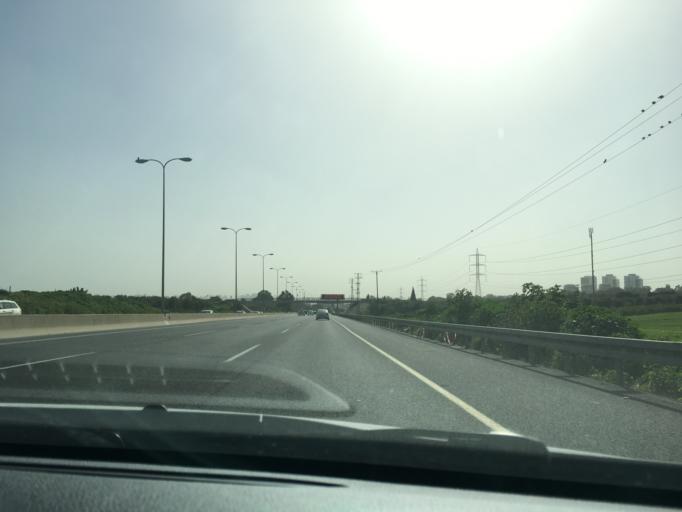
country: IL
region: Central District
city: Hod HaSharon
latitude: 32.1434
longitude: 34.8734
